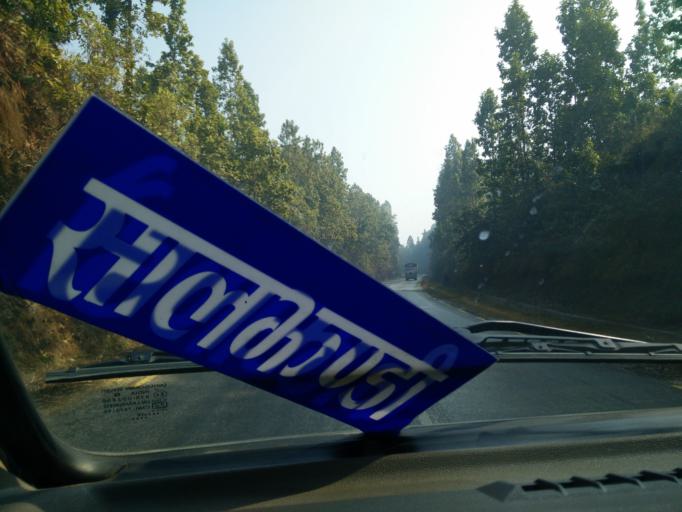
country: NP
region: Central Region
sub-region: Narayani Zone
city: Bharatpur
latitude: 27.6173
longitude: 84.0212
